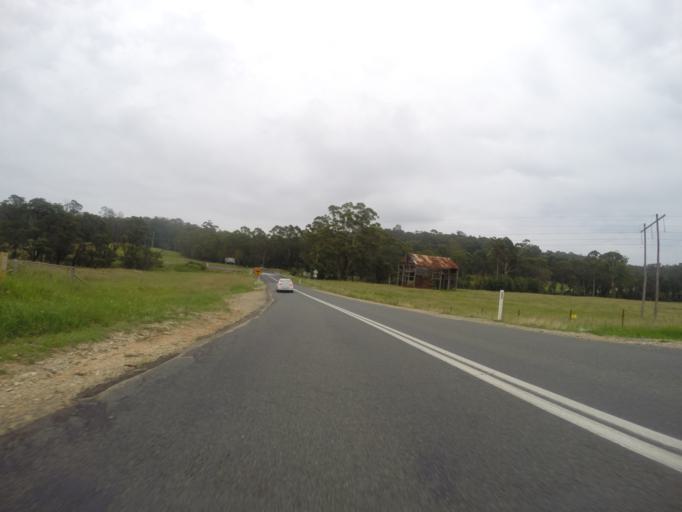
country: AU
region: New South Wales
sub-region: Eurobodalla
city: Batemans Bay
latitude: -35.6481
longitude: 150.2422
